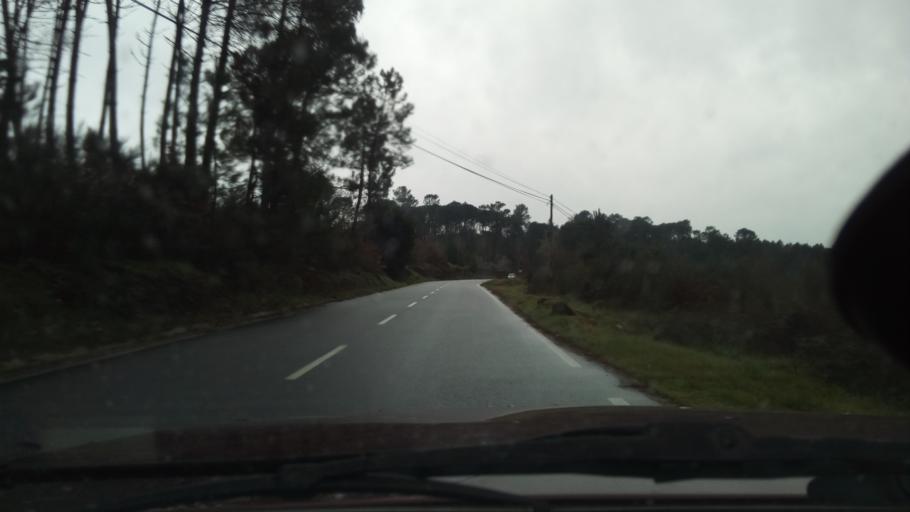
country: PT
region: Viseu
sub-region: Mangualde
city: Mangualde
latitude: 40.6144
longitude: -7.8102
